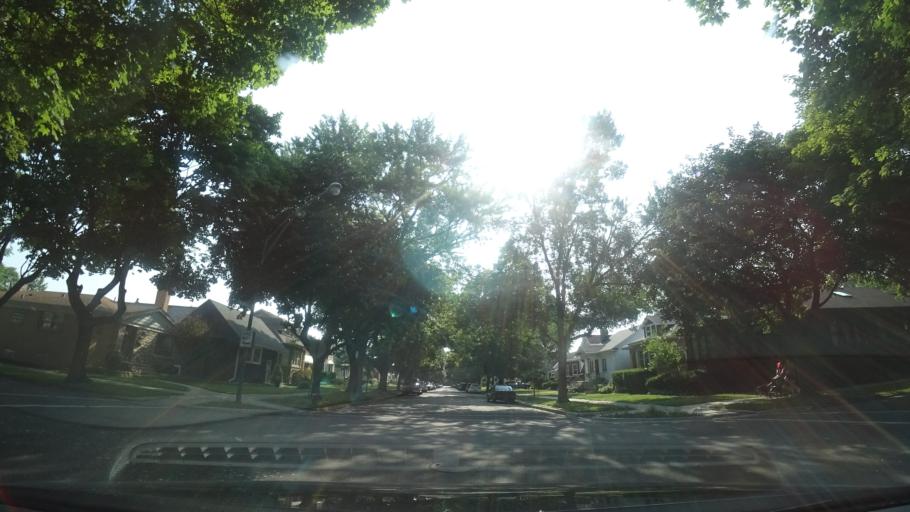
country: US
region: Illinois
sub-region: Cook County
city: Lincolnwood
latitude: 41.9790
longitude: -87.7523
